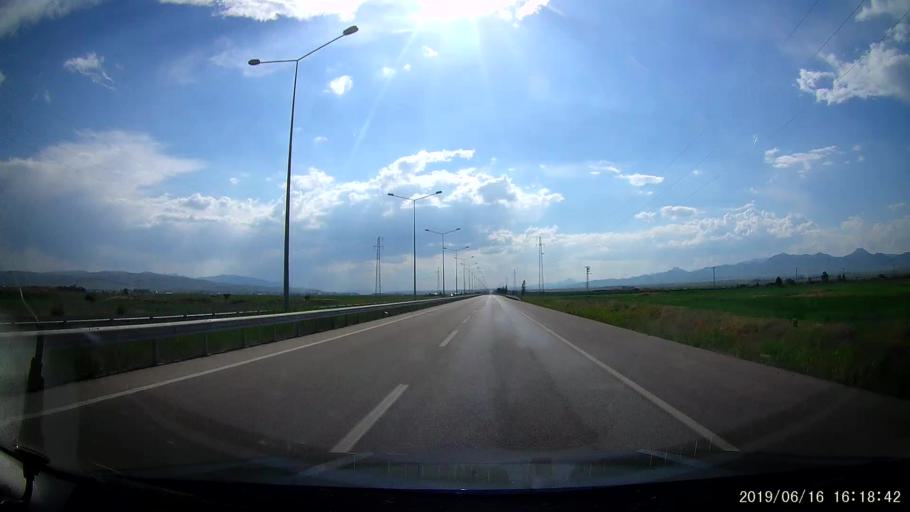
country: TR
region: Erzurum
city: Ilica
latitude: 39.9652
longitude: 41.1610
